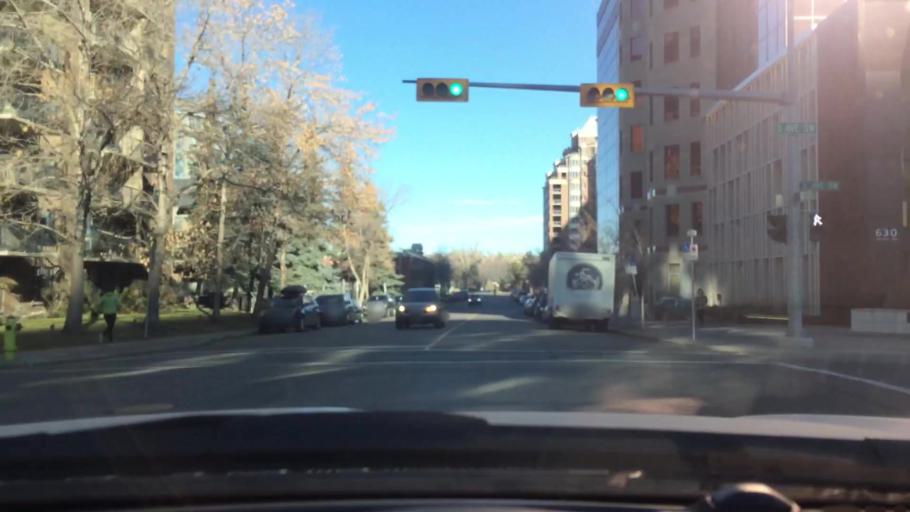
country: CA
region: Alberta
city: Calgary
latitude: 51.0506
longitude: -114.0760
